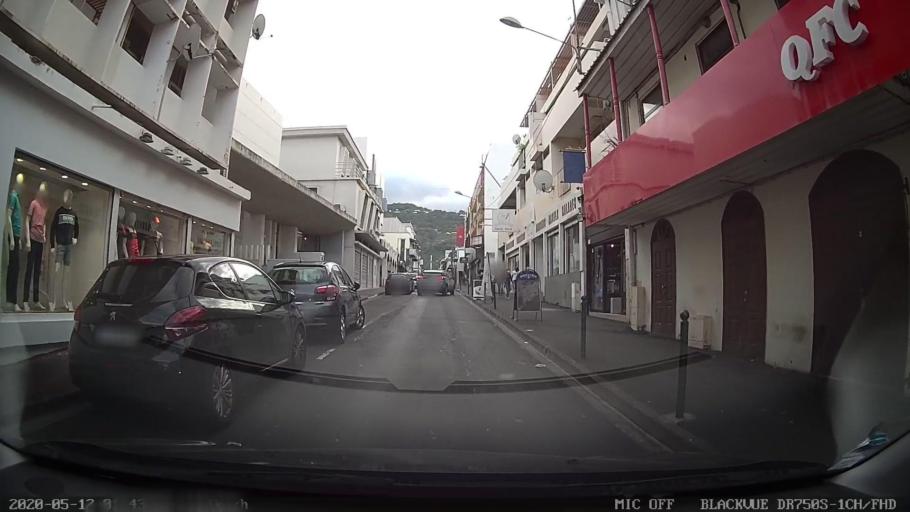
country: RE
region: Reunion
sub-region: Reunion
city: Saint-Denis
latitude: -20.8779
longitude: 55.4510
